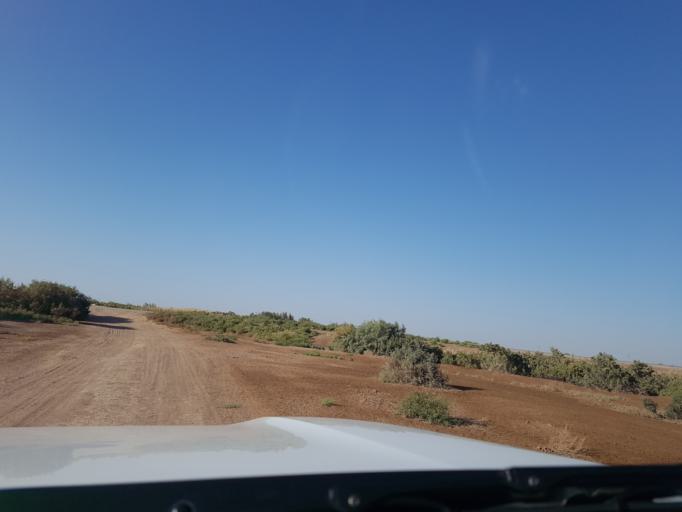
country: IR
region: Razavi Khorasan
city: Sarakhs
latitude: 36.9954
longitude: 61.3881
